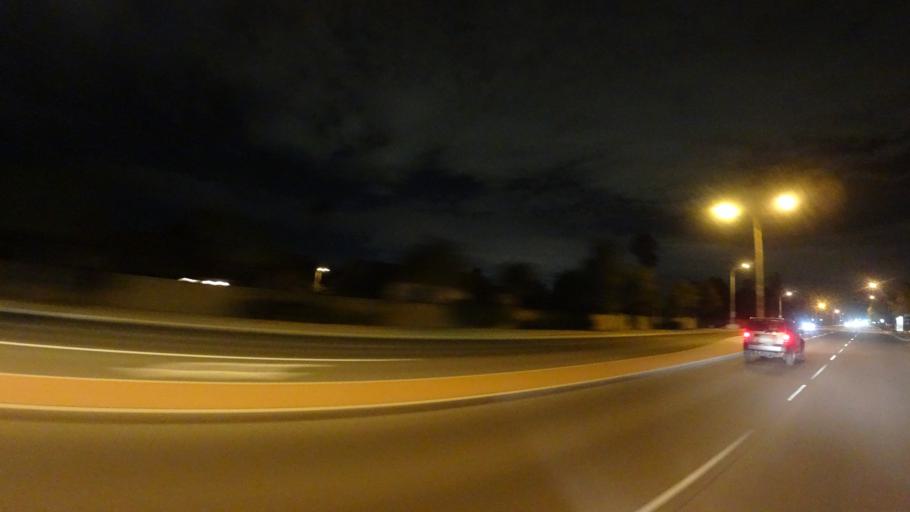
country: US
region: Arizona
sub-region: Maricopa County
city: San Carlos
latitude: 33.3266
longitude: -111.9111
